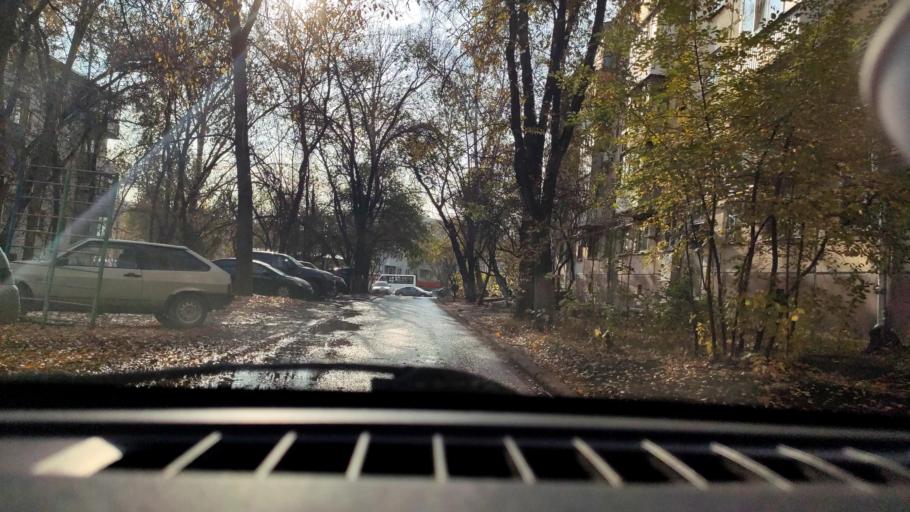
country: RU
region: Samara
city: Samara
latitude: 53.1929
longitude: 50.2070
